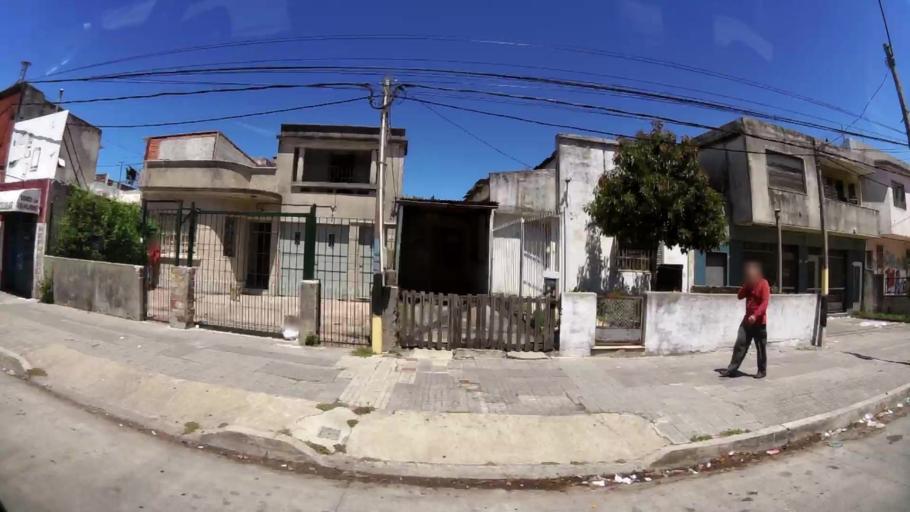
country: UY
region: Montevideo
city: Montevideo
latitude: -34.8914
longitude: -56.1258
